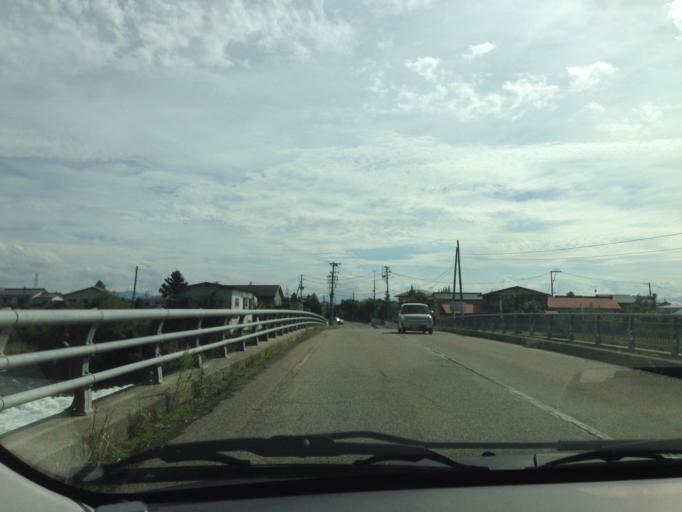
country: JP
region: Fukushima
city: Kitakata
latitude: 37.5819
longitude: 139.9133
